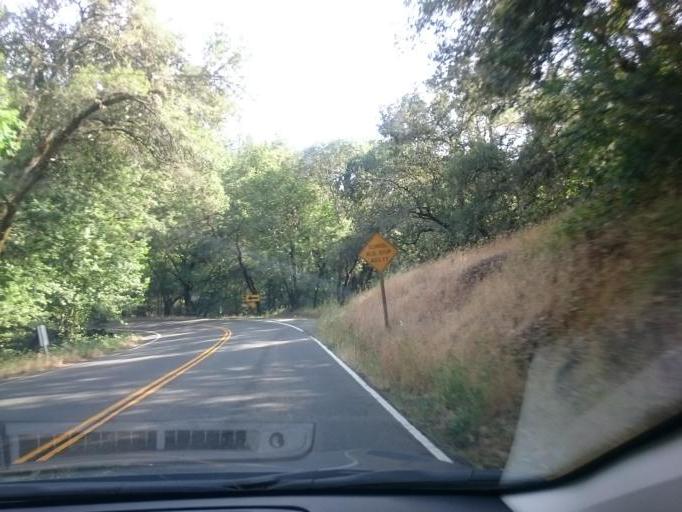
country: US
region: California
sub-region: Napa County
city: Calistoga
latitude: 38.6033
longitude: -122.6458
